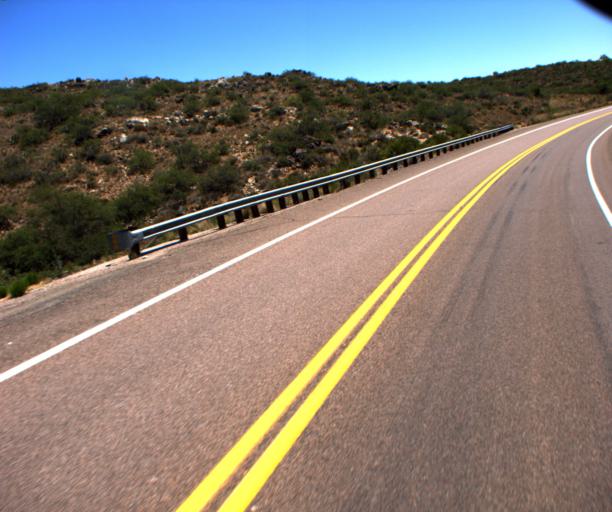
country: US
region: Arizona
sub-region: Yavapai County
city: Bagdad
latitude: 34.5479
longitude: -113.1490
